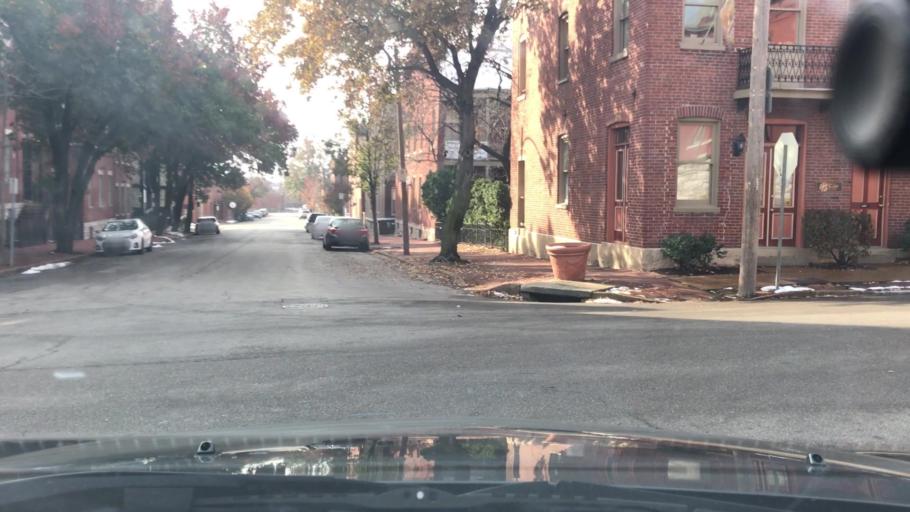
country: US
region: Missouri
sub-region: City of Saint Louis
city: St. Louis
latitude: 38.6082
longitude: -90.2033
